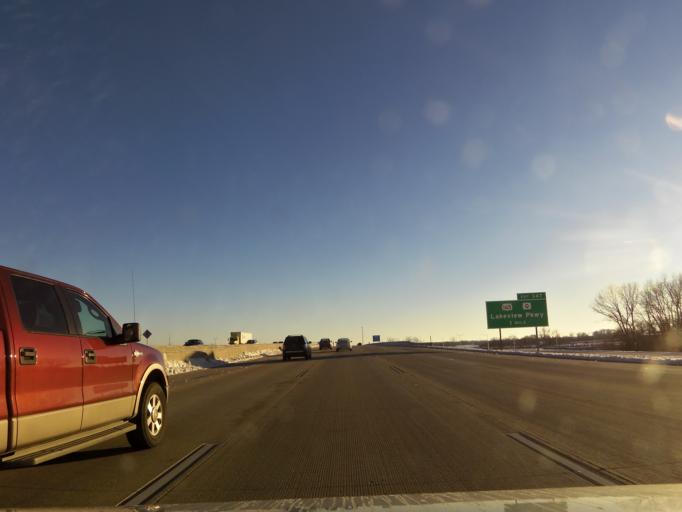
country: US
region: Wisconsin
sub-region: Kenosha County
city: Pleasant Prairie
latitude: 42.5465
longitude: -87.9525
